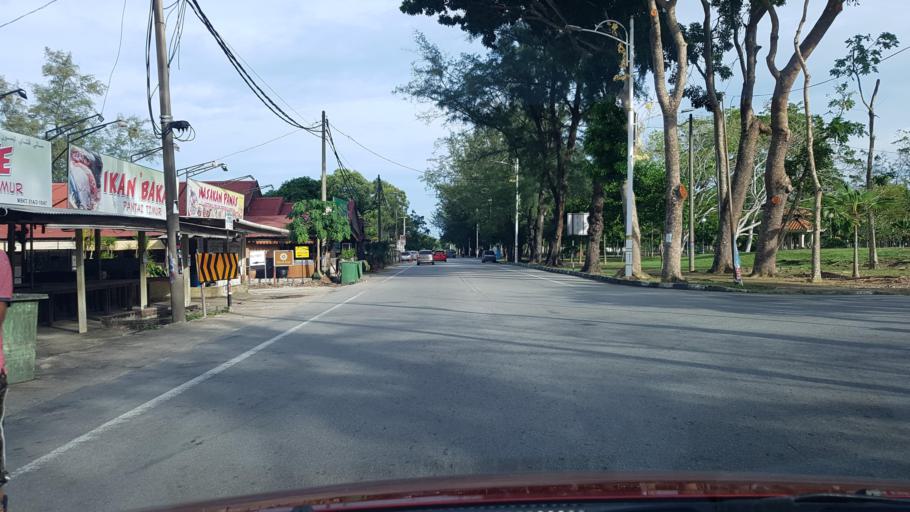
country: MY
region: Terengganu
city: Kuala Terengganu
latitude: 5.3204
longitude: 103.1552
